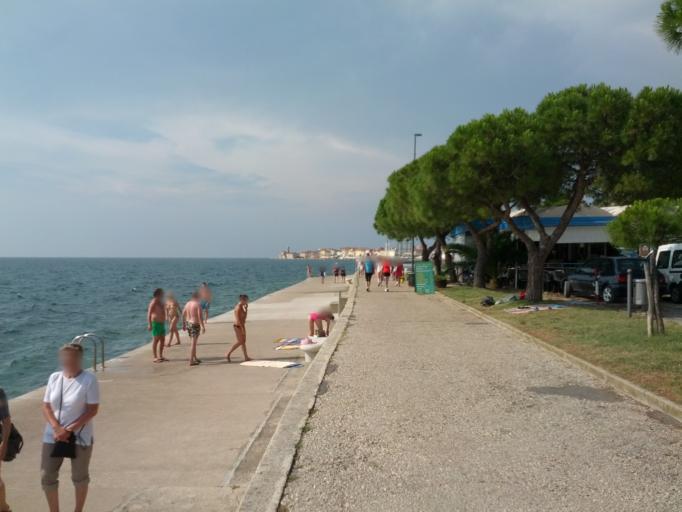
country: SI
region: Piran-Pirano
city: Piran
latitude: 45.5212
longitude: 13.5666
